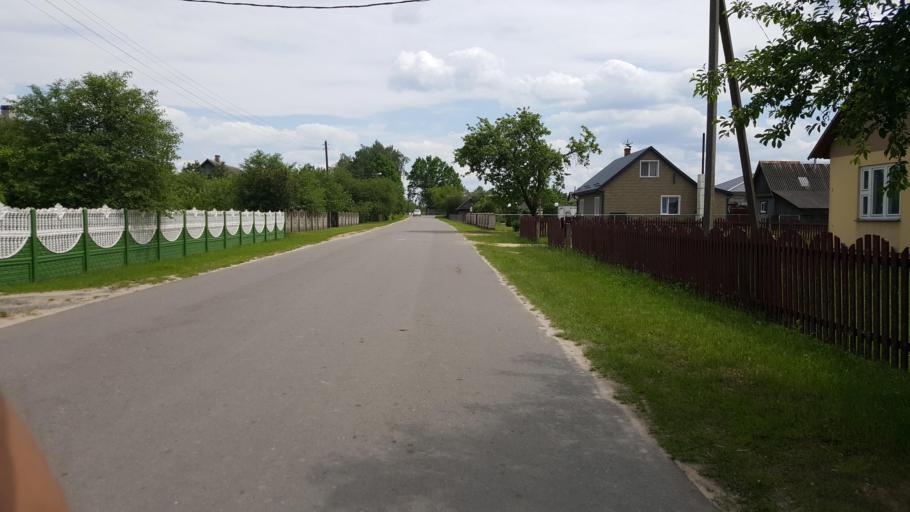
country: PL
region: Podlasie
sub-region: Powiat hajnowski
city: Bialowieza
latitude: 52.6719
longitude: 24.0820
